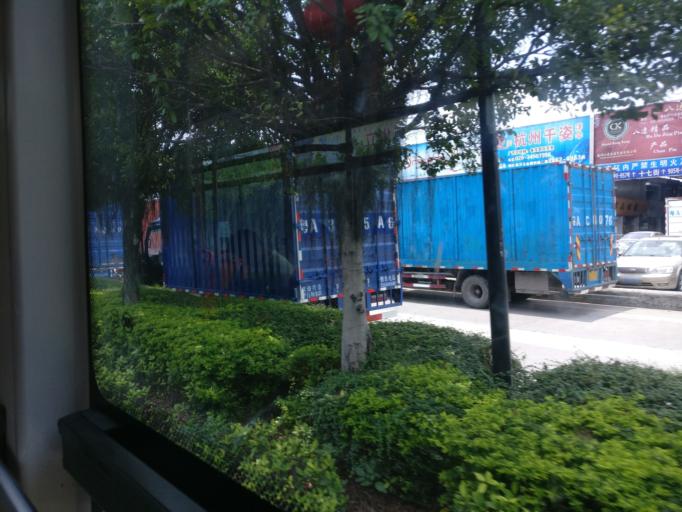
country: CN
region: Guangdong
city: Dashi
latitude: 23.0370
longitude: 113.3317
